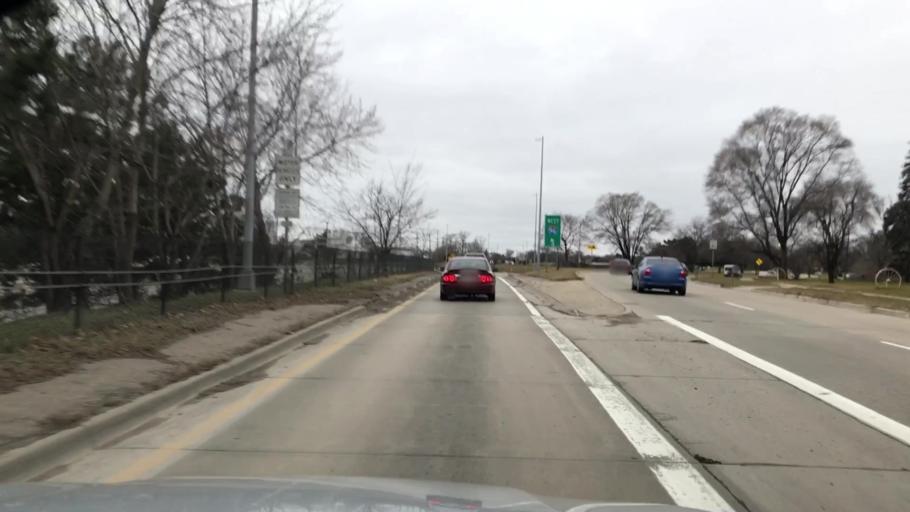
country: US
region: Michigan
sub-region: Wayne County
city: Plymouth
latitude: 42.3820
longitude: -83.4168
